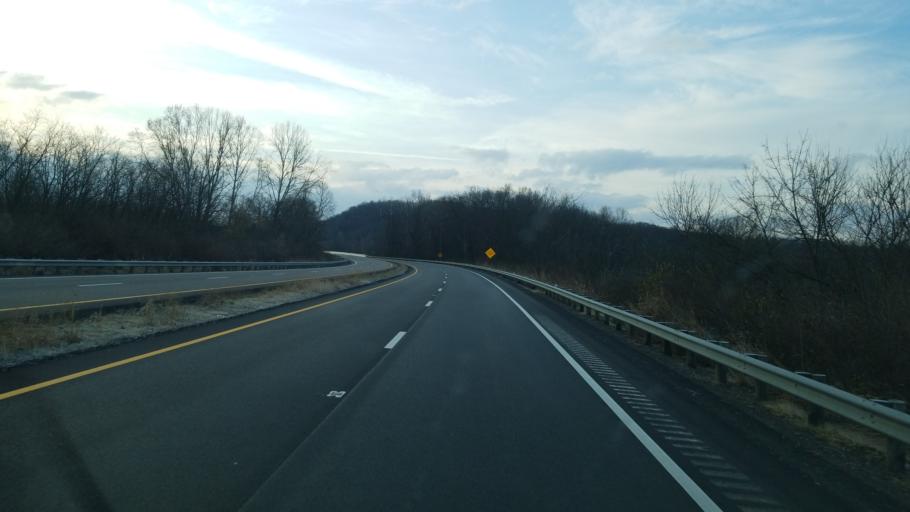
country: US
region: Ohio
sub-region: Ross County
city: Chillicothe
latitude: 39.3111
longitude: -82.9612
